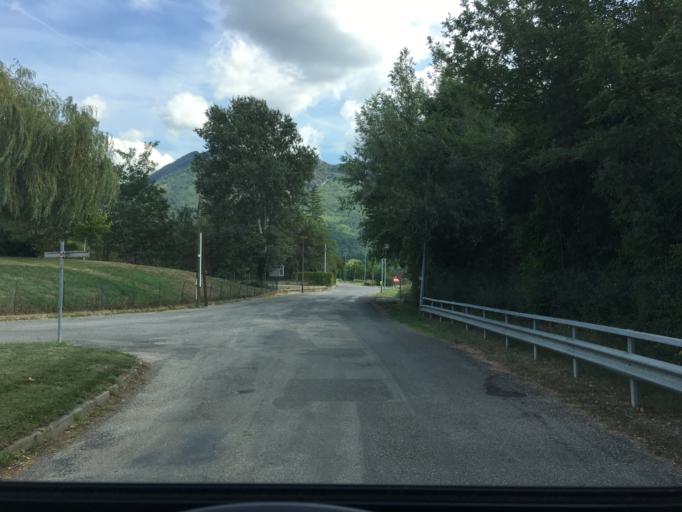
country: FR
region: Provence-Alpes-Cote d'Azur
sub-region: Departement des Alpes-de-Haute-Provence
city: Sisteron
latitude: 44.2143
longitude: 5.9362
